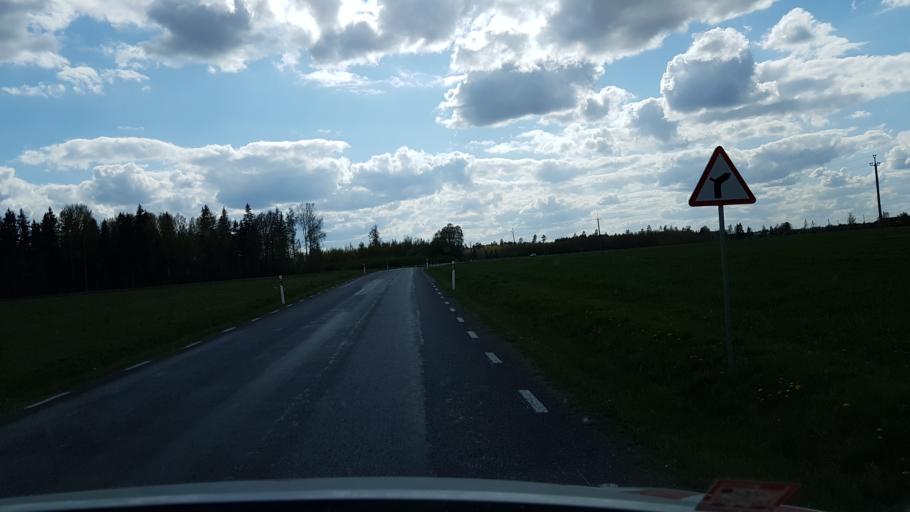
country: EE
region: Tartu
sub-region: Tartu linn
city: Tartu
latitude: 58.3973
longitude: 26.8628
